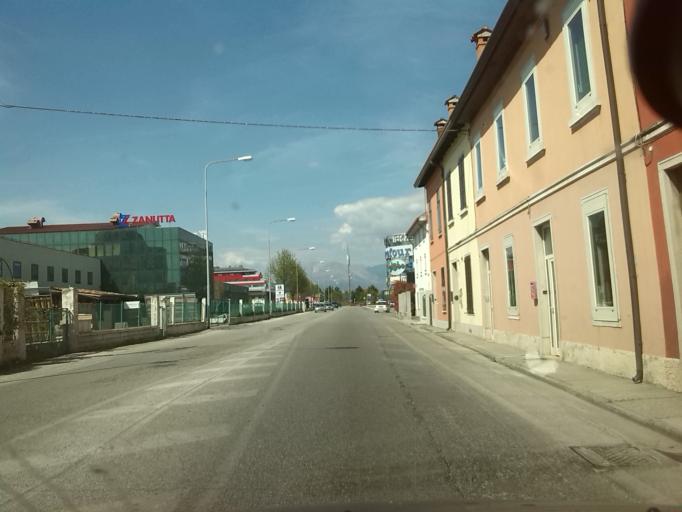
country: IT
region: Friuli Venezia Giulia
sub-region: Provincia di Udine
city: Feletto Umberto
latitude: 46.0915
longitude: 13.2319
